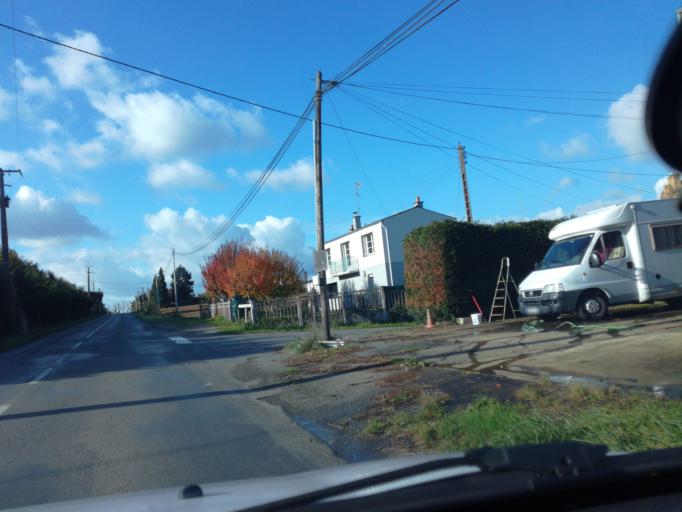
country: FR
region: Brittany
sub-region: Departement d'Ille-et-Vilaine
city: Chavagne
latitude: 48.0280
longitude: -1.7904
